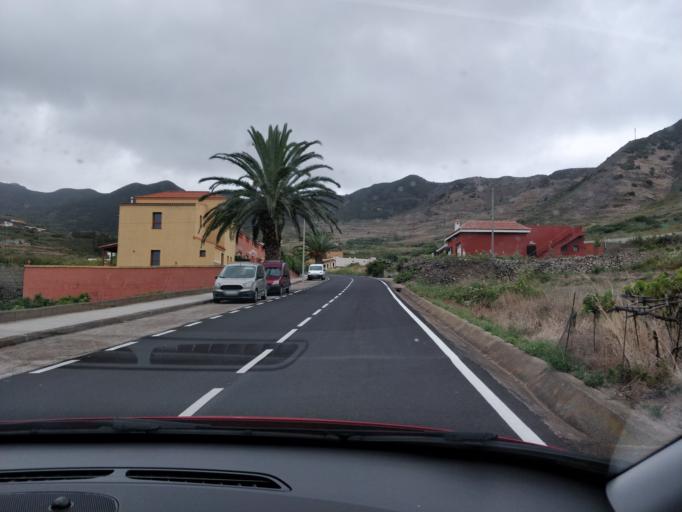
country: ES
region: Canary Islands
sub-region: Provincia de Santa Cruz de Tenerife
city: Tanque
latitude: 28.3368
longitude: -16.8518
